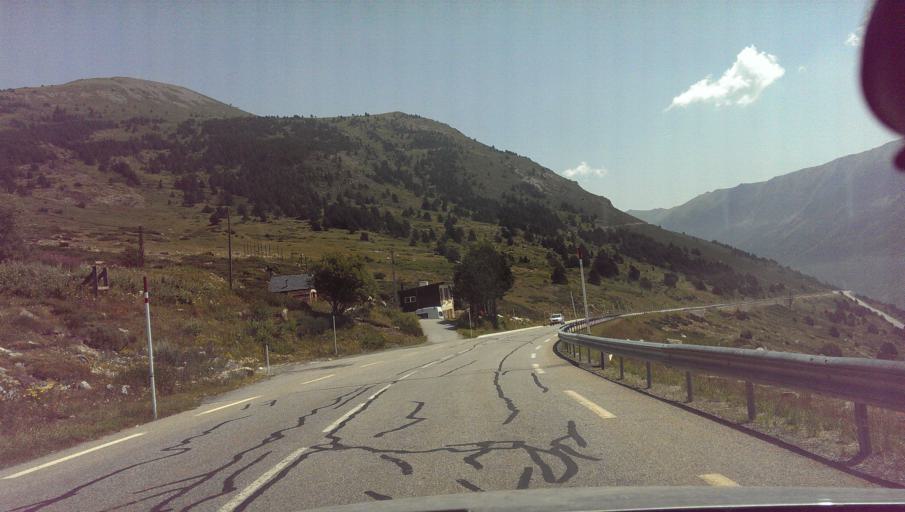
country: AD
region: Encamp
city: Pas de la Casa
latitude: 42.5594
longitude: 1.8122
